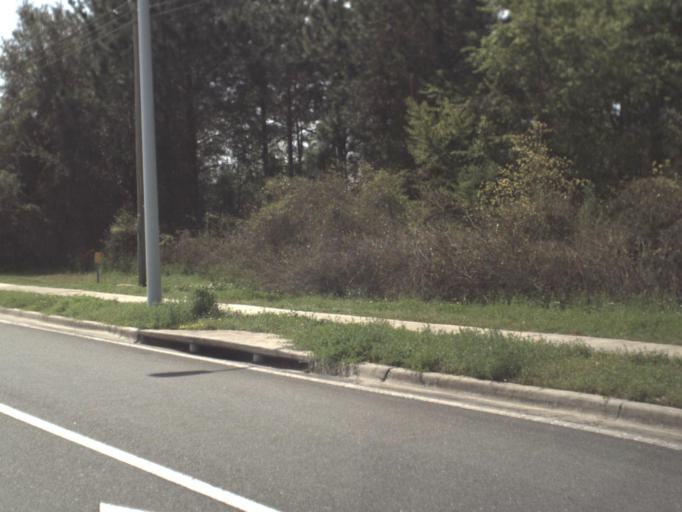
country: US
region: Florida
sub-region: Leon County
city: Tallahassee
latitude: 30.3997
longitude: -84.2351
